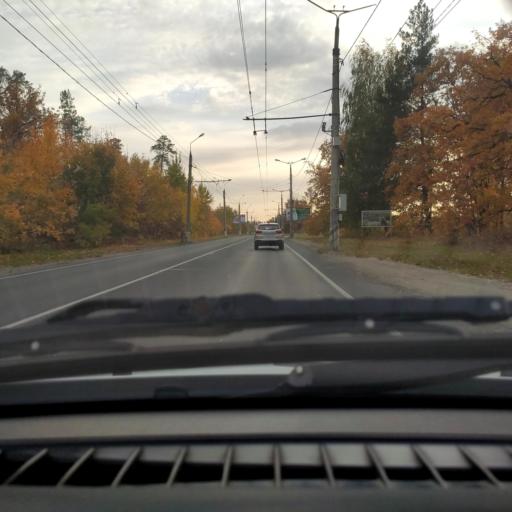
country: RU
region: Samara
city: Tol'yatti
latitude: 53.4892
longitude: 49.3843
